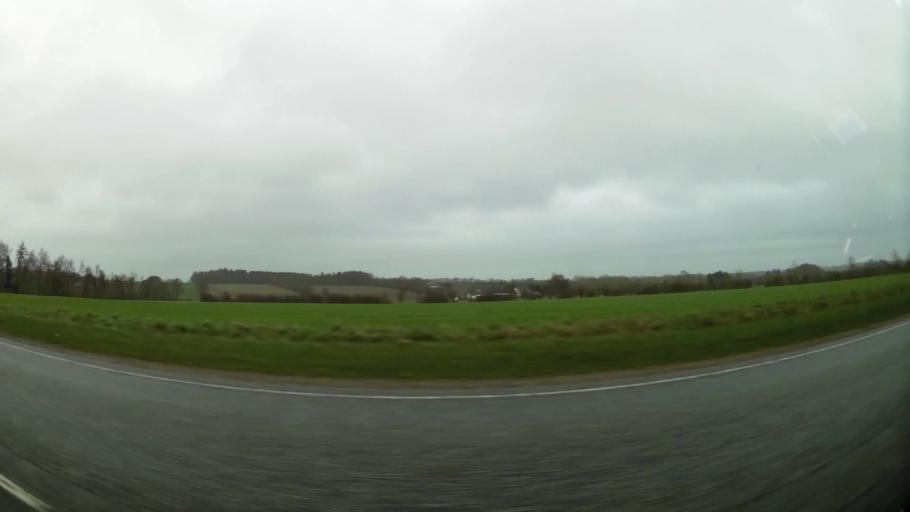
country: DK
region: Central Jutland
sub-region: Herning Kommune
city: Avlum
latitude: 56.2736
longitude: 8.7623
